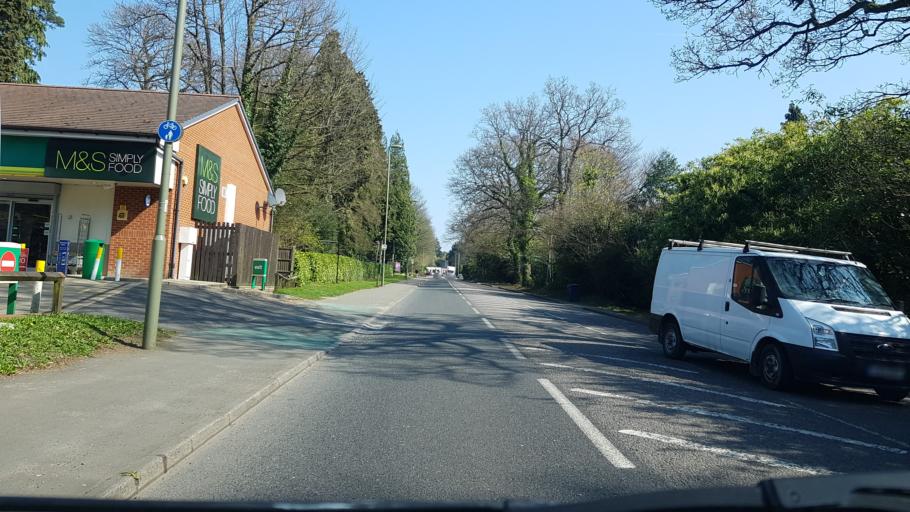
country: GB
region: England
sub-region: Surrey
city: Hindhead
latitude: 51.1110
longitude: -0.7378
